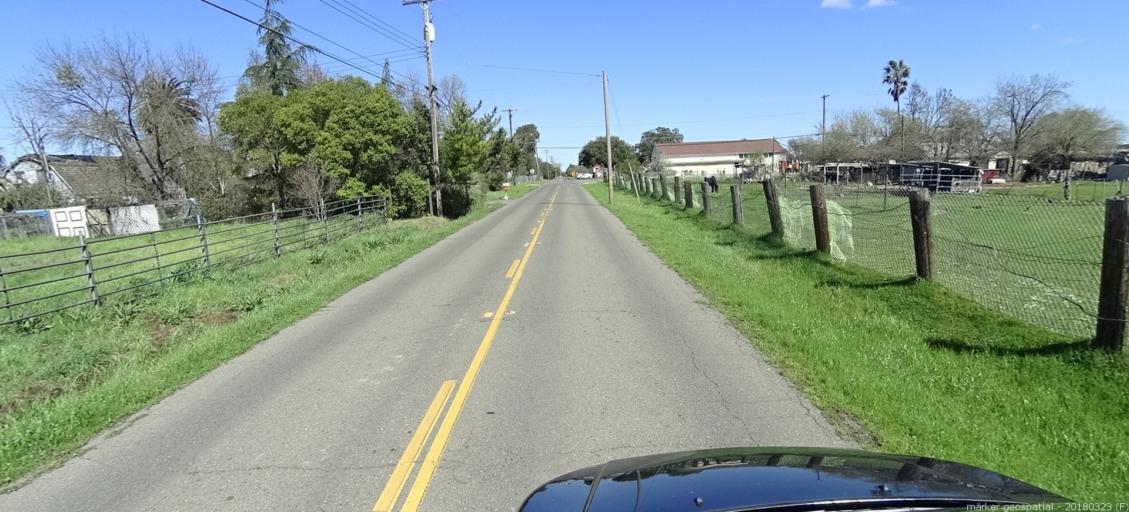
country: US
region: California
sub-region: Sacramento County
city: Rio Linda
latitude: 38.6827
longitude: -121.4198
